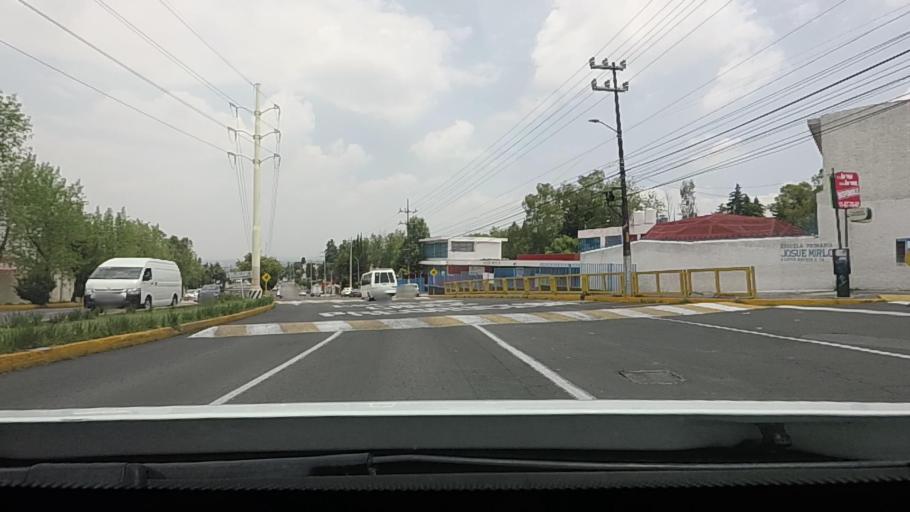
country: MX
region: Mexico
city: Naucalpan de Juarez
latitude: 19.5057
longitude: -99.2517
